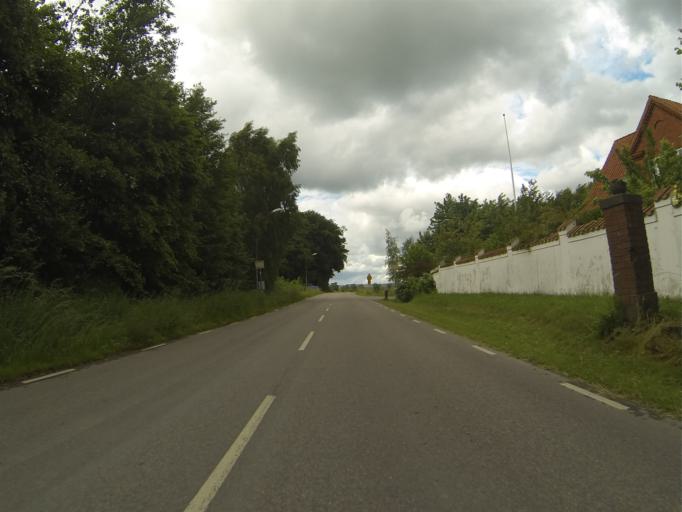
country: SE
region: Skane
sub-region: Lunds Kommun
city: Veberod
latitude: 55.6813
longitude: 13.4240
